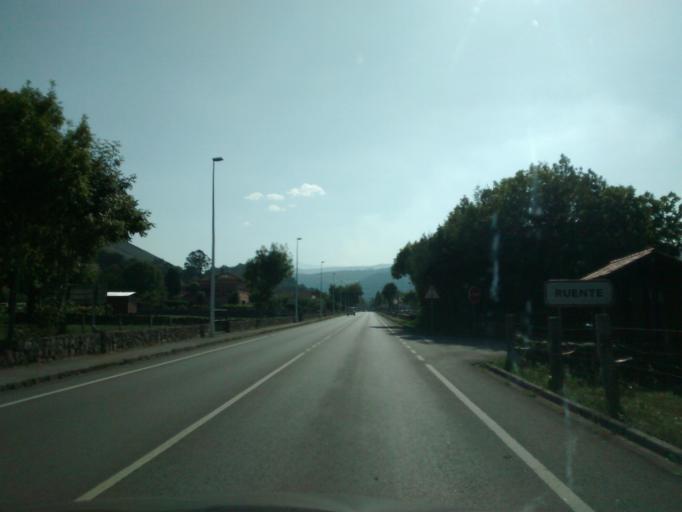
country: ES
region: Cantabria
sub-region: Provincia de Cantabria
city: Ruente
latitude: 43.2630
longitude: -4.2605
